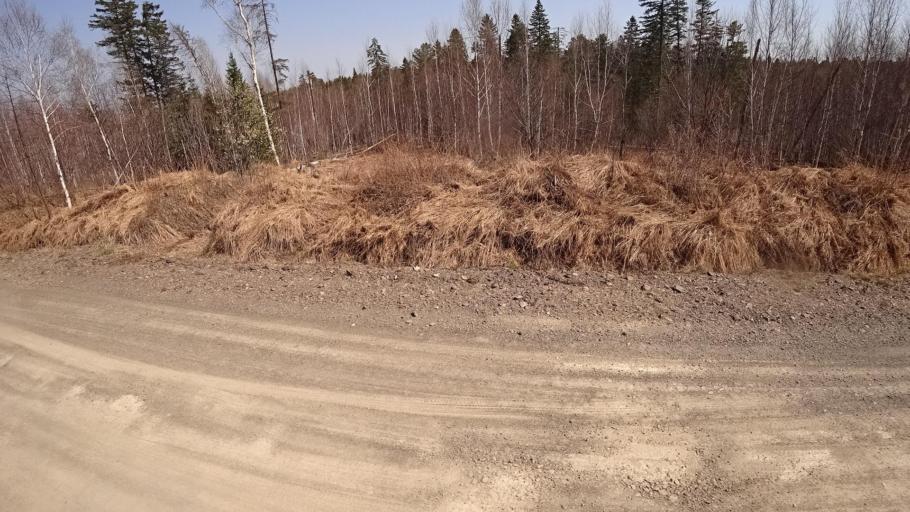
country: RU
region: Khabarovsk Krai
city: Selikhino
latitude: 50.6247
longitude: 137.4018
